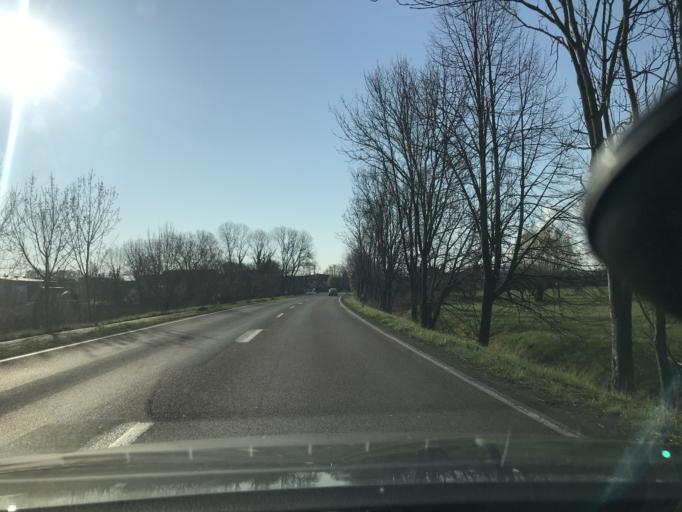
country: DE
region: Saxony-Anhalt
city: Holleben
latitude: 51.4262
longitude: 11.9227
